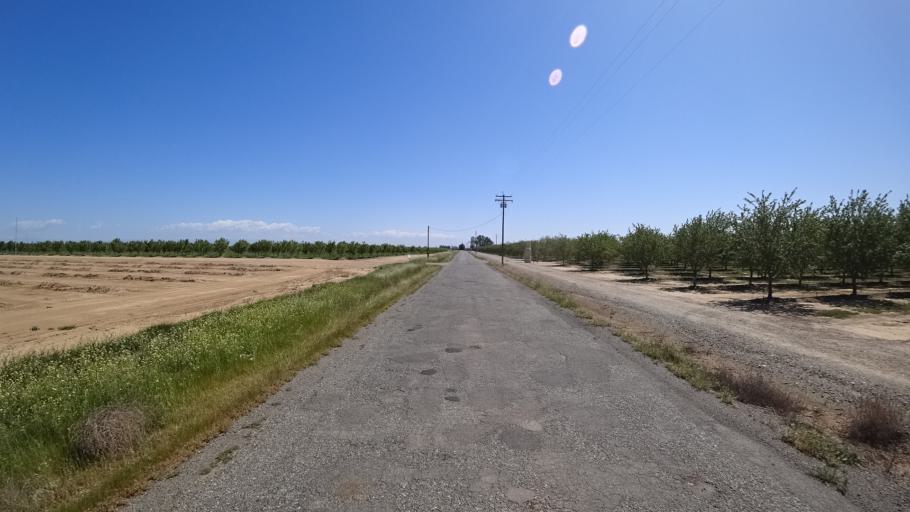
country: US
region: California
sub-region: Glenn County
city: Orland
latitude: 39.6816
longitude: -122.1456
